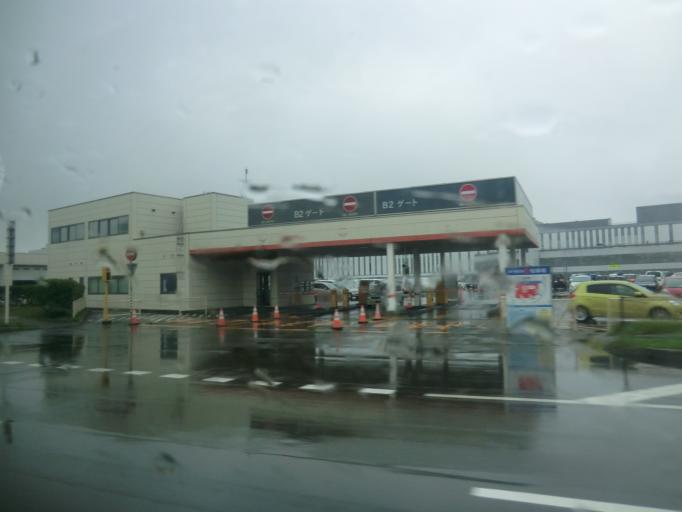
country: JP
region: Hokkaido
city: Chitose
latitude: 42.7857
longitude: 141.6797
